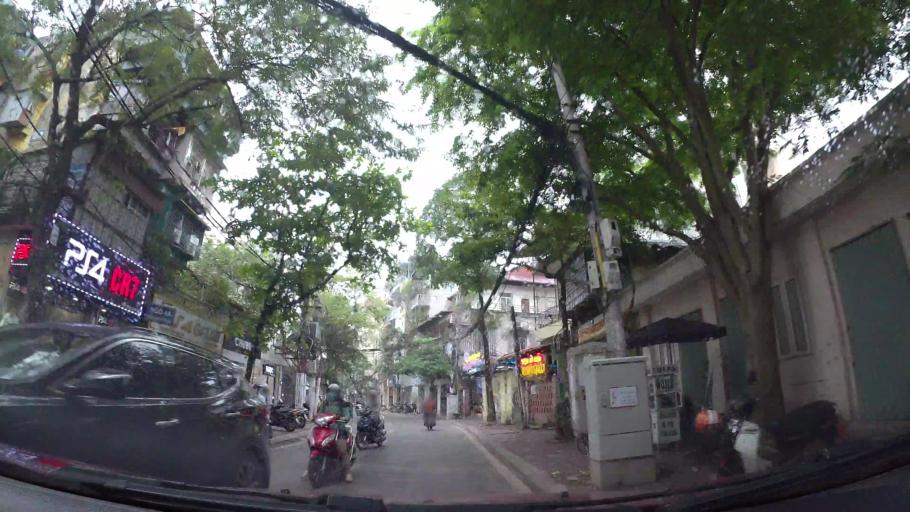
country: VN
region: Ha Noi
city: Dong Da
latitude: 21.0089
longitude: 105.8317
